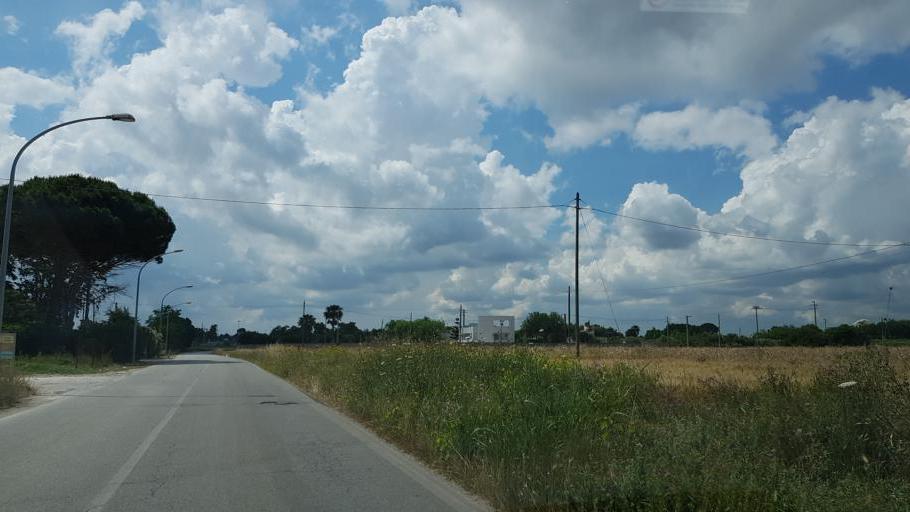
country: IT
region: Apulia
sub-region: Provincia di Brindisi
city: Mesagne
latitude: 40.5470
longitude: 17.8141
